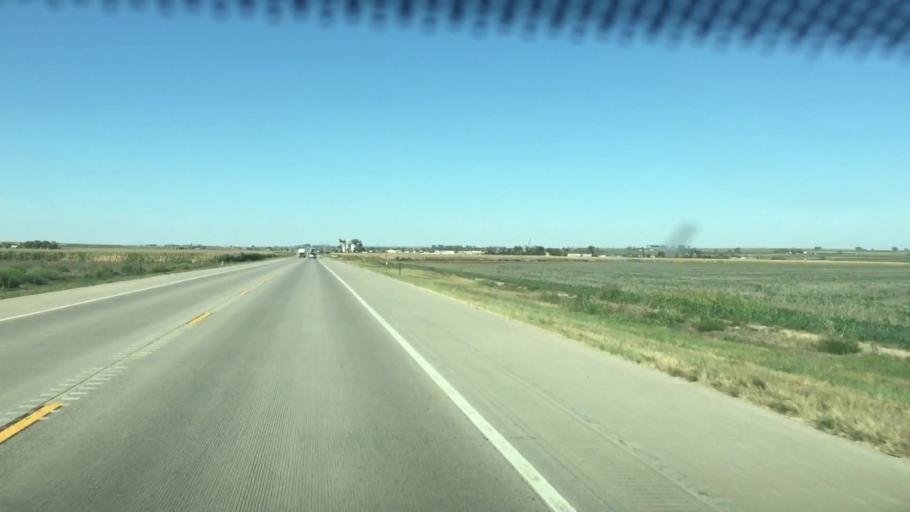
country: US
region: Colorado
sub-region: Prowers County
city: Lamar
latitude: 38.1314
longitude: -102.7237
